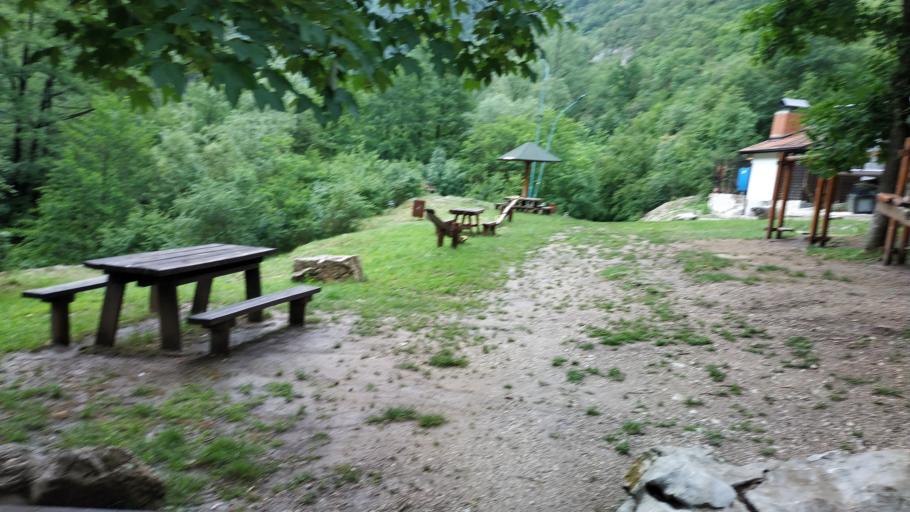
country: RS
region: Central Serbia
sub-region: Zajecarski Okrug
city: Soko Banja
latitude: 43.6368
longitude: 21.8880
